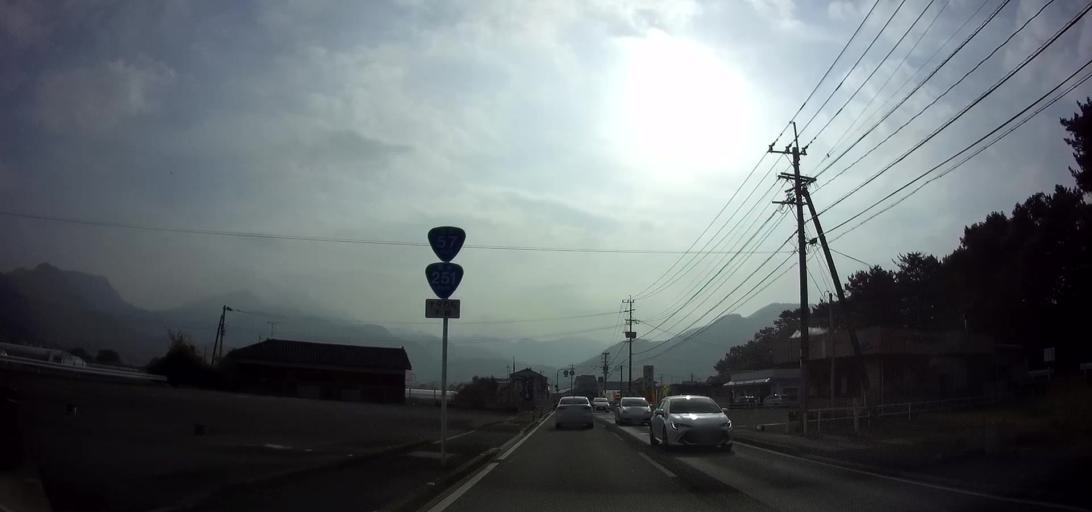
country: JP
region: Nagasaki
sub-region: Isahaya-shi
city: Isahaya
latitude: 32.7909
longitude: 130.1865
